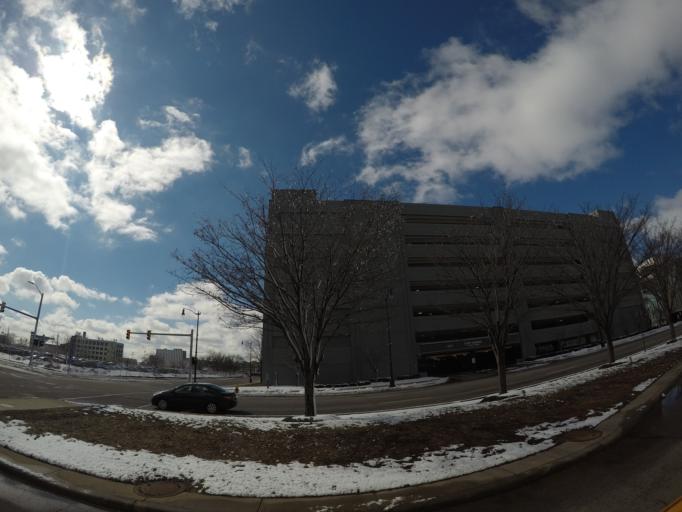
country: US
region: Michigan
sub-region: Wayne County
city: Detroit
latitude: 42.3296
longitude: -83.0558
